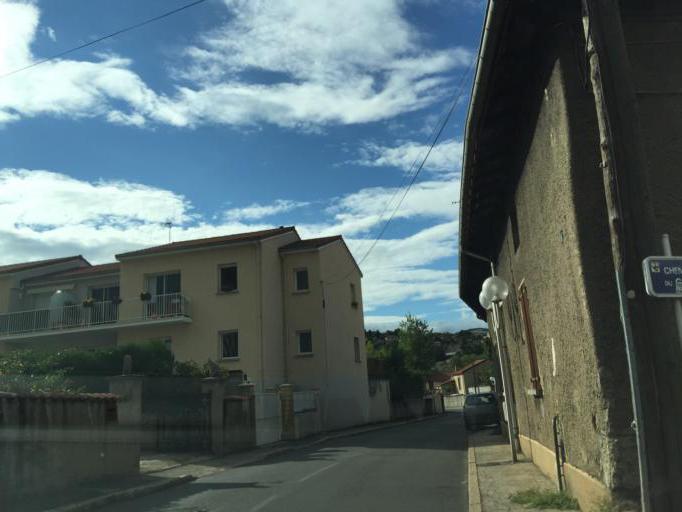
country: FR
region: Rhone-Alpes
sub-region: Departement de la Loire
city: La Grand-Croix
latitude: 45.4951
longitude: 4.5591
